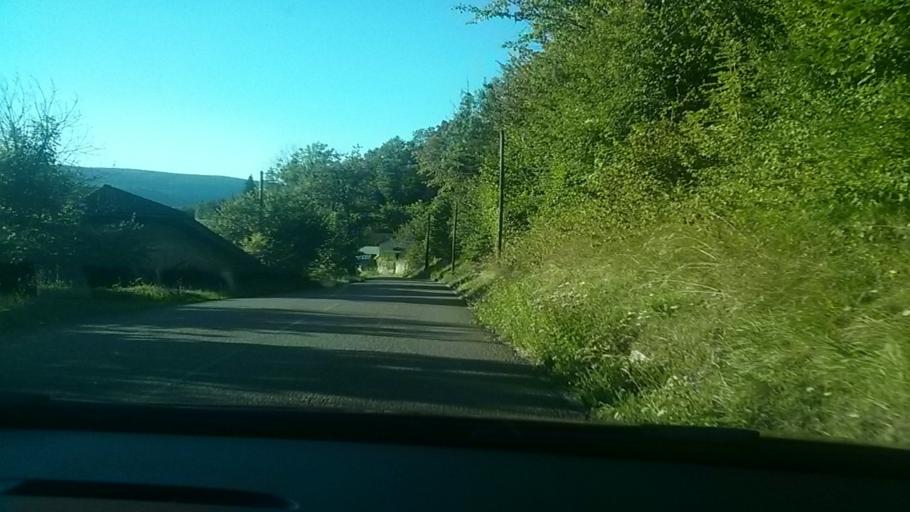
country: FR
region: Franche-Comte
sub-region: Departement du Jura
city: Saint-Claude
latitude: 46.3656
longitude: 5.8837
